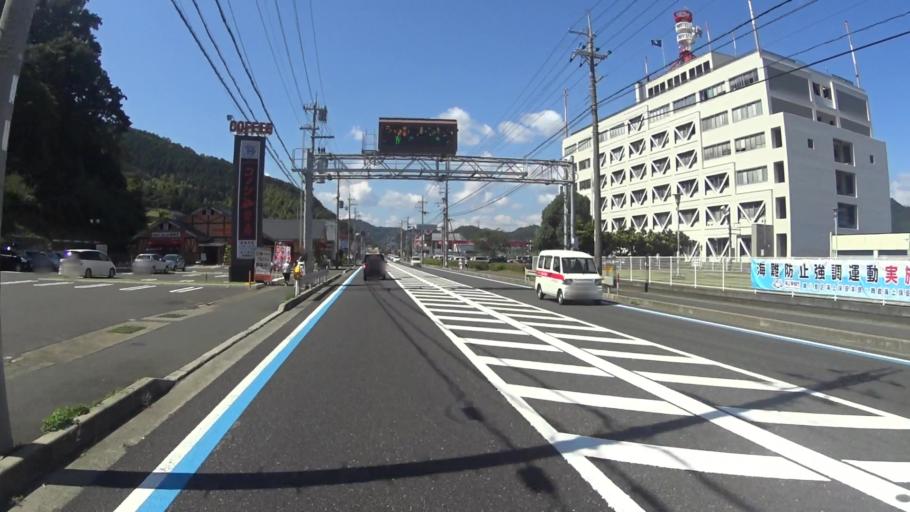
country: JP
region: Kyoto
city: Maizuru
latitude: 35.4504
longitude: 135.3188
